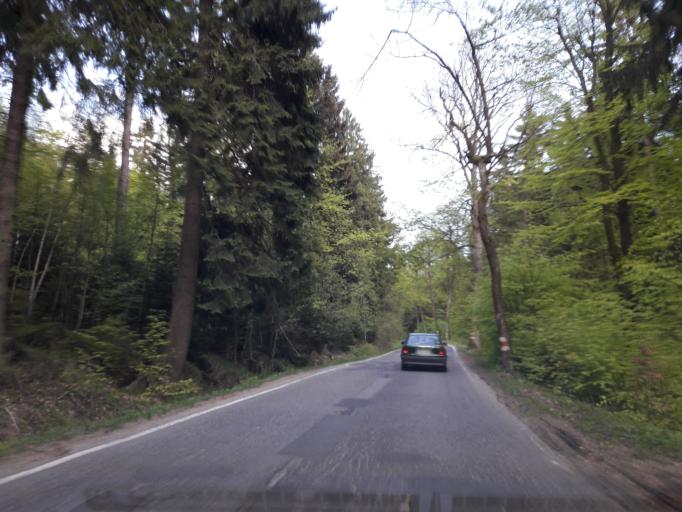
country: CZ
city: Machov
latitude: 50.4644
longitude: 16.3217
